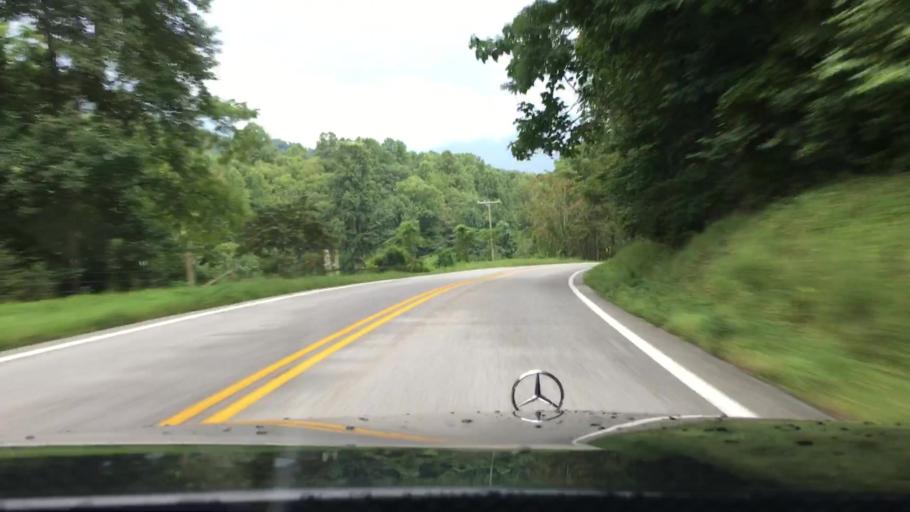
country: US
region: Virginia
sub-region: Nelson County
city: Nellysford
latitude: 37.8371
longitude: -78.9281
